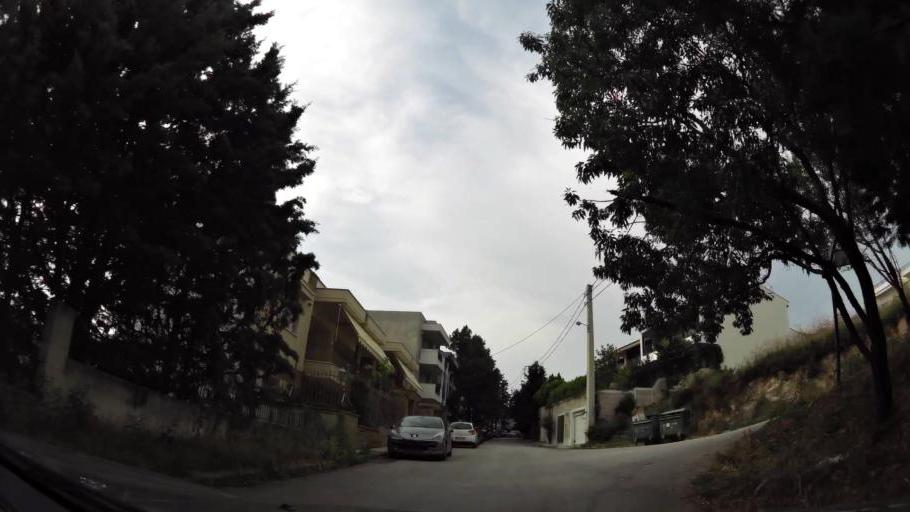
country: GR
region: Central Macedonia
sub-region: Nomos Thessalonikis
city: Oraiokastro
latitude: 40.7337
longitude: 22.9224
